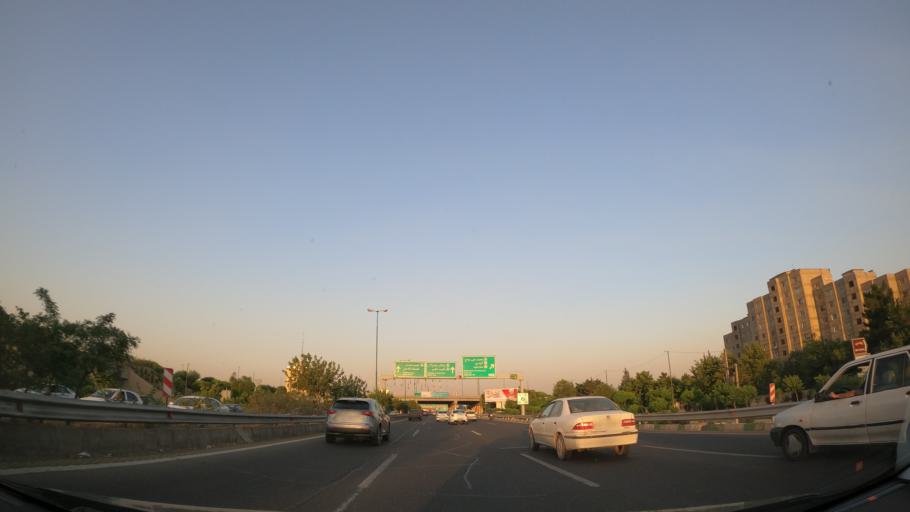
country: IR
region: Tehran
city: Tehran
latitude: 35.7140
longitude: 51.3271
